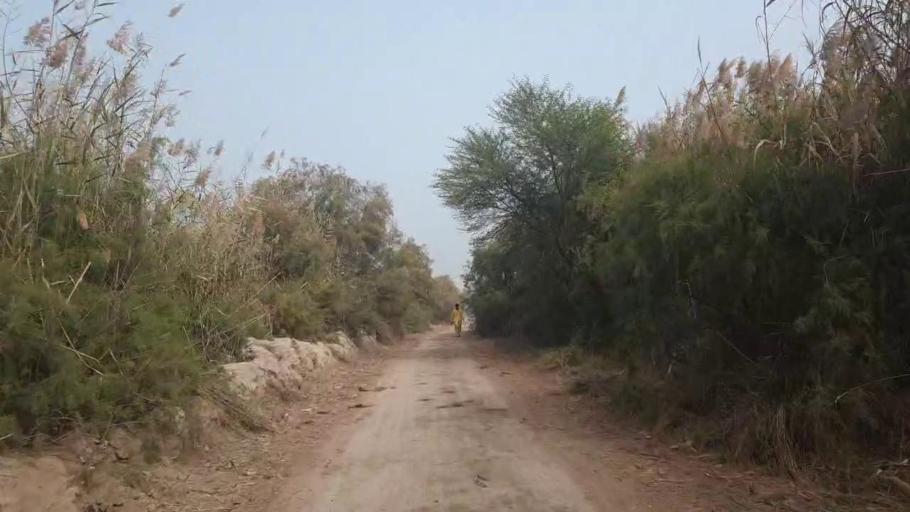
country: PK
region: Sindh
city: Bhit Shah
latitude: 25.8198
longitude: 68.5636
